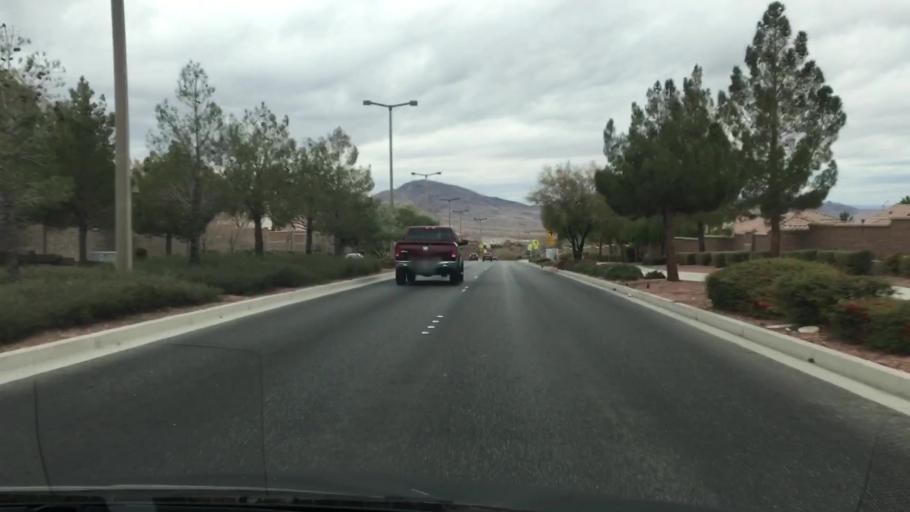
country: US
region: Nevada
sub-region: Clark County
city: Whitney
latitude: 35.9437
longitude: -115.1008
